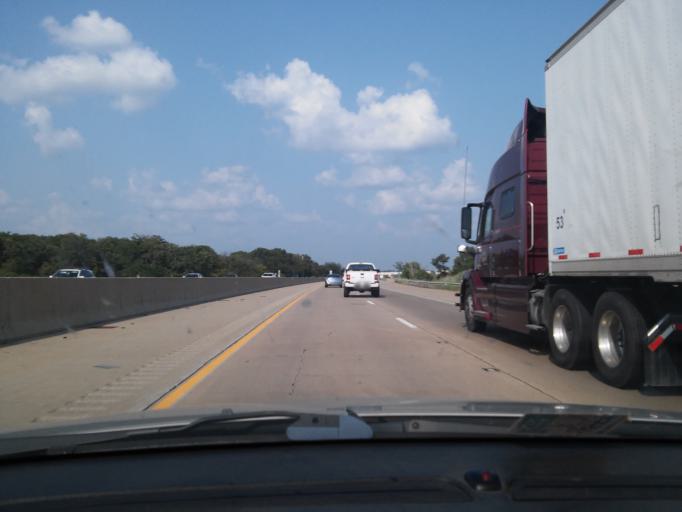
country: US
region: Illinois
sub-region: Grundy County
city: Minooka
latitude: 41.4590
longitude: -88.3094
